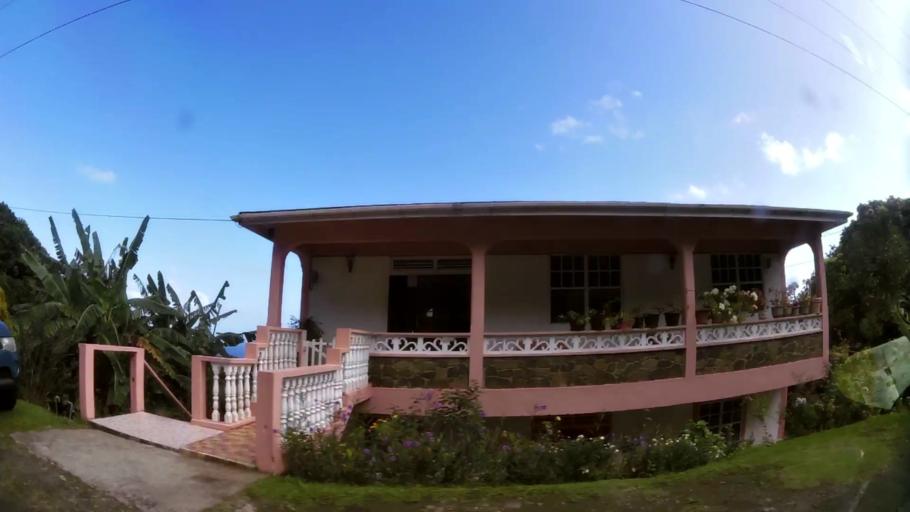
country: DM
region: Saint Andrew
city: Marigot
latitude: 15.5158
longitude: -61.2628
